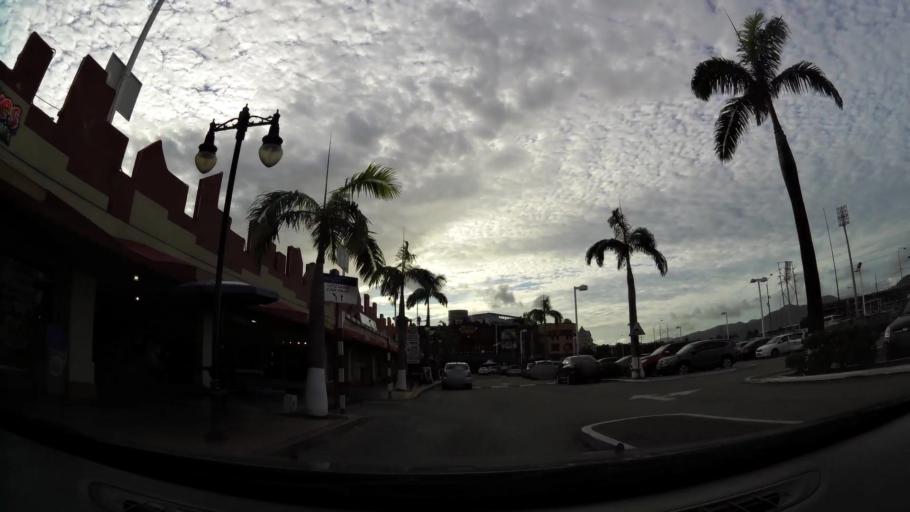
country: TT
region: City of Port of Spain
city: Mucurapo
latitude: 10.6589
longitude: -61.5318
